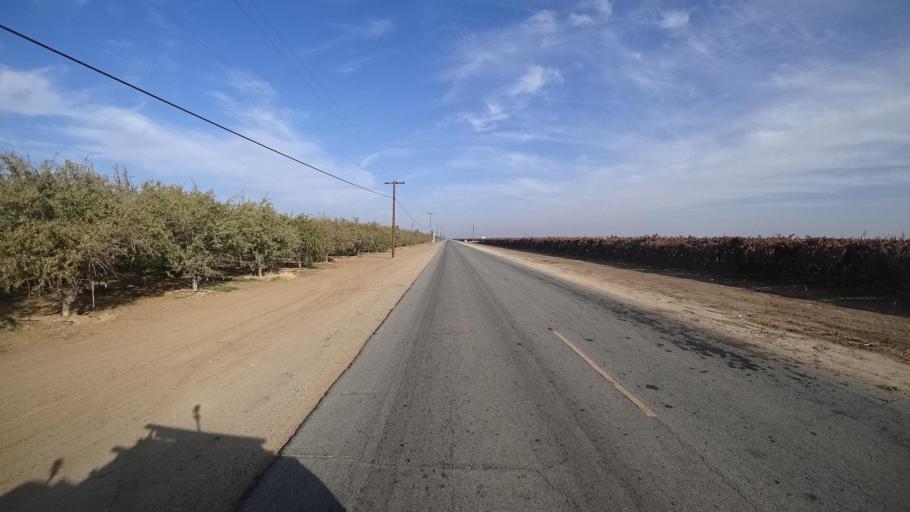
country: US
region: California
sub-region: Kern County
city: McFarland
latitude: 35.6654
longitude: -119.2047
